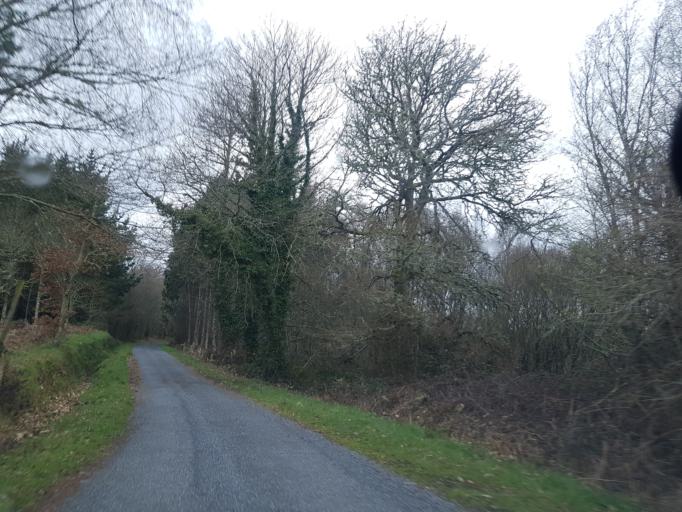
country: ES
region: Galicia
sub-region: Provincia de Lugo
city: Friol
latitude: 43.1216
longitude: -7.8177
